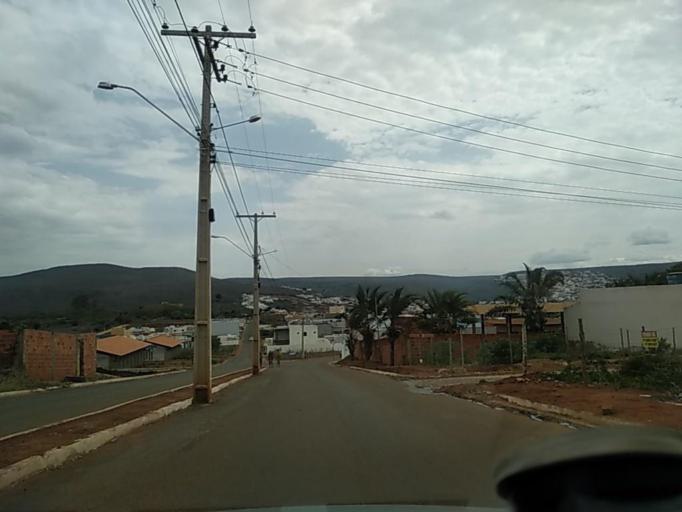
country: BR
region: Bahia
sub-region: Caetite
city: Caetite
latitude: -14.0585
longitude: -42.4726
